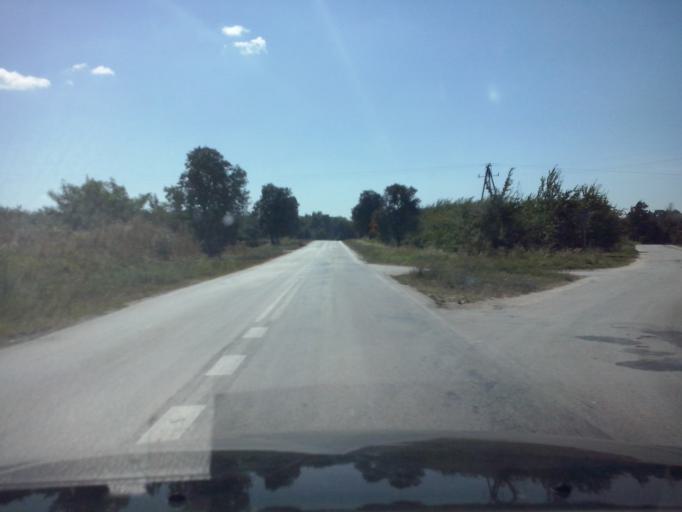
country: PL
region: Swietokrzyskie
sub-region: Powiat staszowski
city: Szydlow
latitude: 50.5979
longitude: 21.0094
